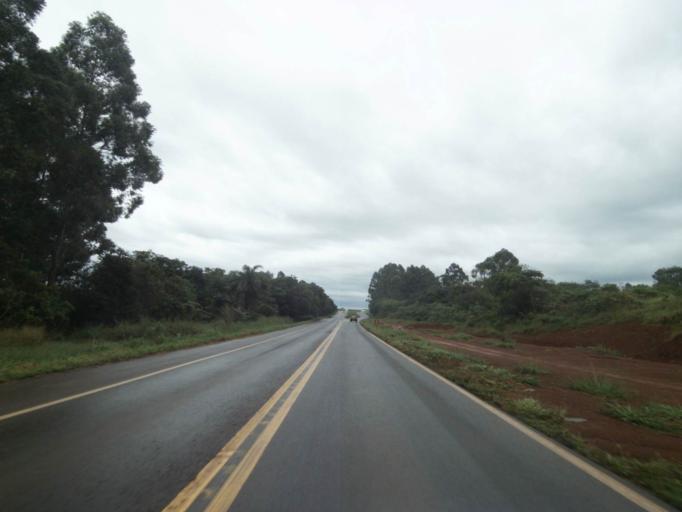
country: BR
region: Parana
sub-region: Toledo
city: Toledo
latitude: -24.6899
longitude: -53.7607
